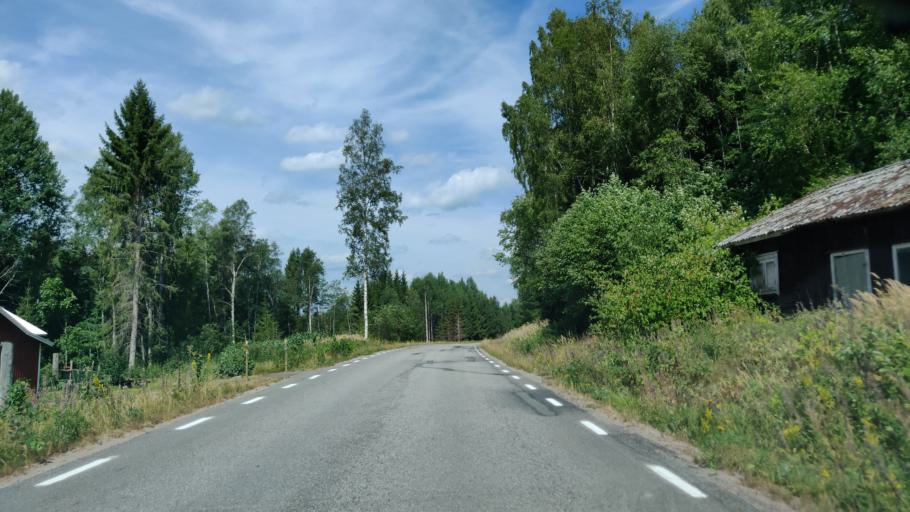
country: SE
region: Vaermland
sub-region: Hagfors Kommun
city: Ekshaerad
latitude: 60.1034
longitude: 13.4999
